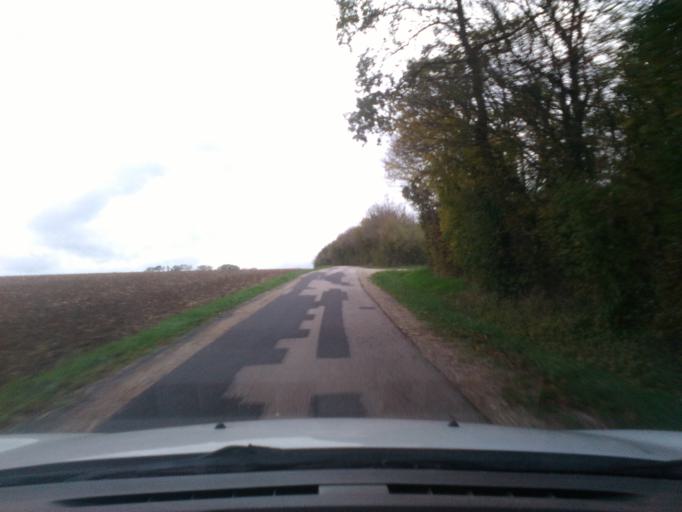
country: FR
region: Lorraine
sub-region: Departement des Vosges
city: Mirecourt
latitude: 48.3384
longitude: 6.1267
